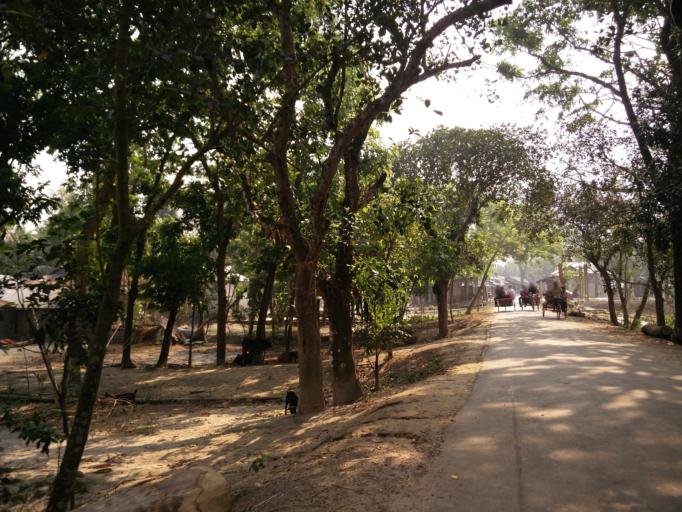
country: BD
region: Dhaka
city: Muktagacha
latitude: 24.9105
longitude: 90.1583
